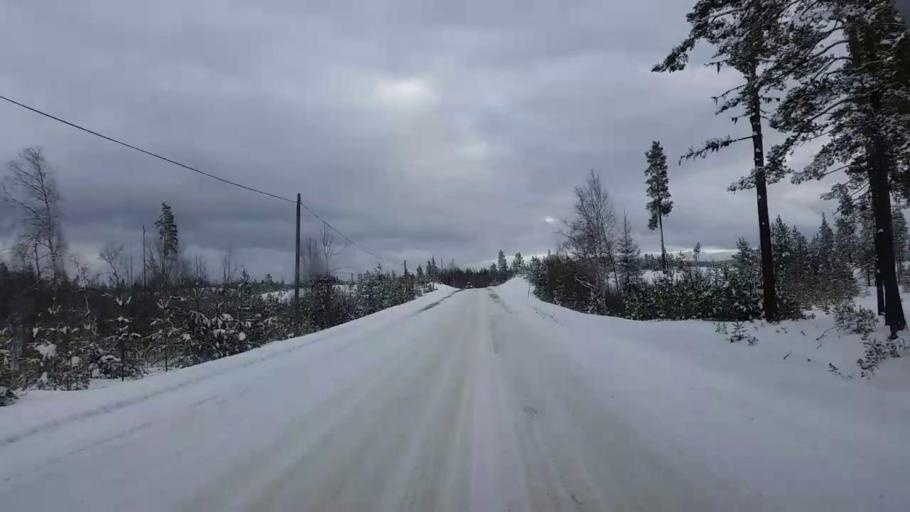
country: SE
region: Jaemtland
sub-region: Harjedalens Kommun
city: Sveg
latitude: 62.1266
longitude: 14.9819
